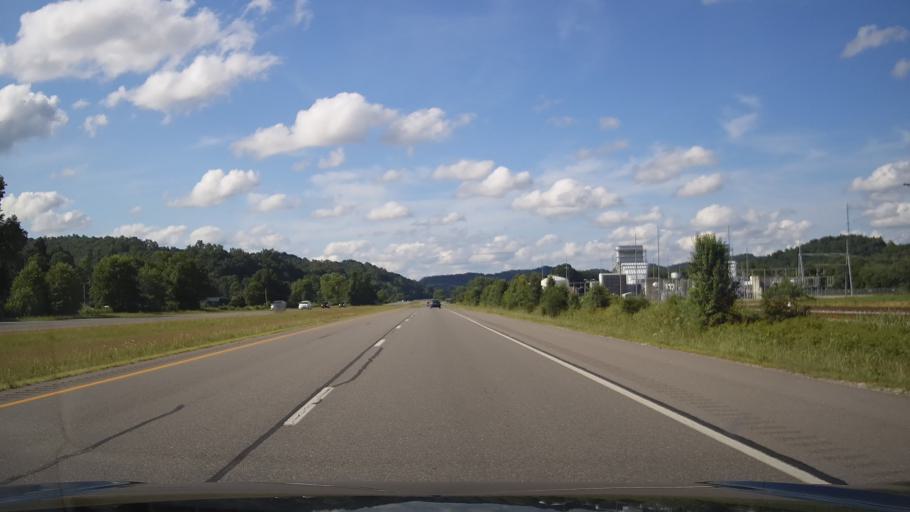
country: US
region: Kentucky
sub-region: Lawrence County
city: Louisa
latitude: 38.1877
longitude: -82.6069
